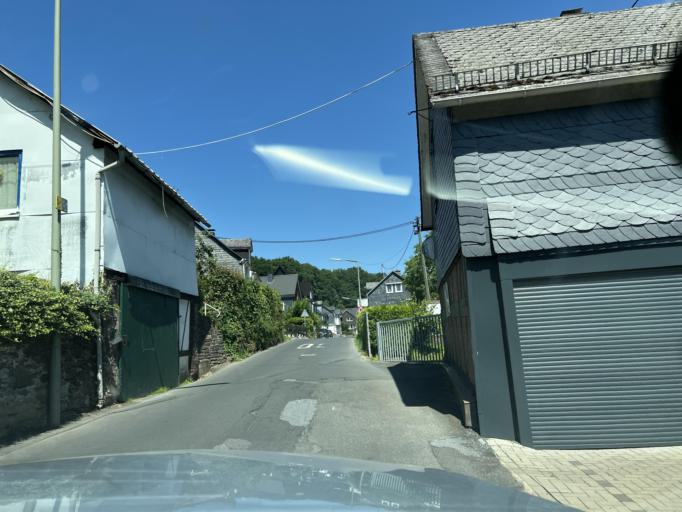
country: DE
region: North Rhine-Westphalia
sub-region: Regierungsbezirk Arnsberg
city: Siegen
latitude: 50.8921
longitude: 7.9821
